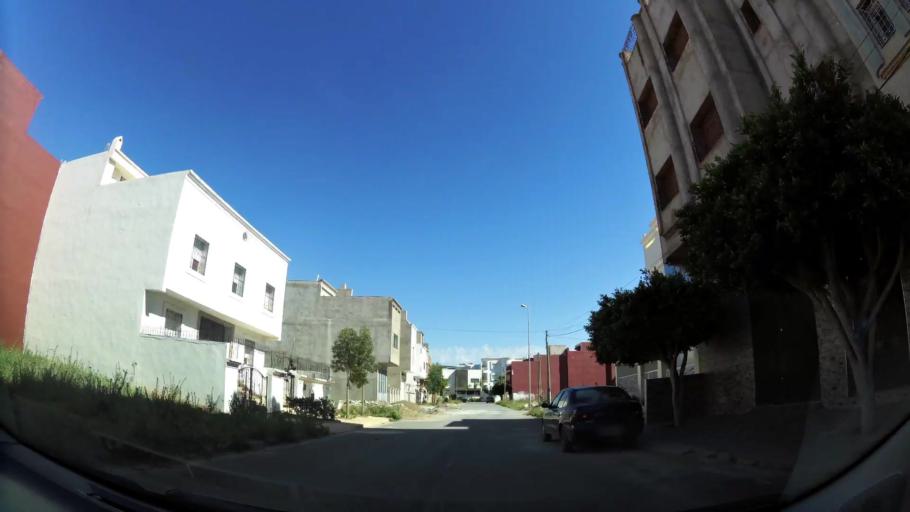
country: MA
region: Oriental
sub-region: Berkane-Taourirt
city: Berkane
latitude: 34.9457
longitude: -2.3344
